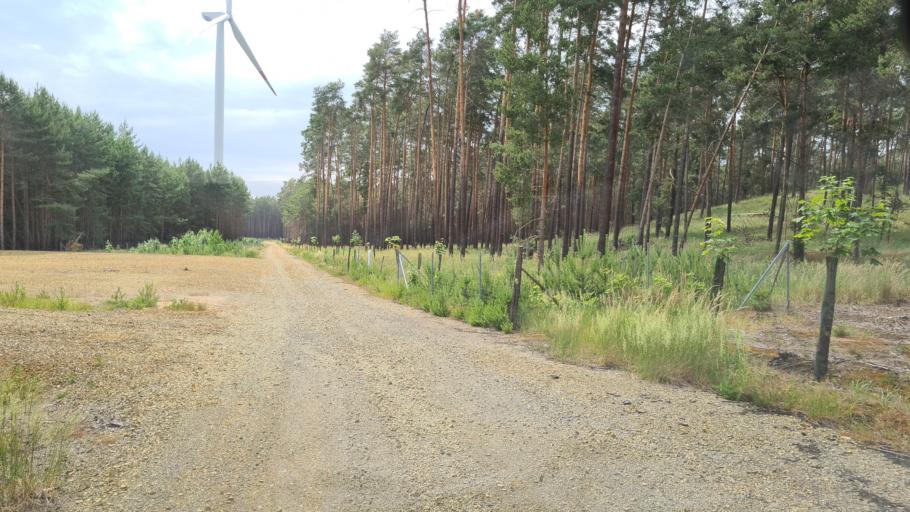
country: DE
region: Brandenburg
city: Schlieben
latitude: 51.6639
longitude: 13.3538
